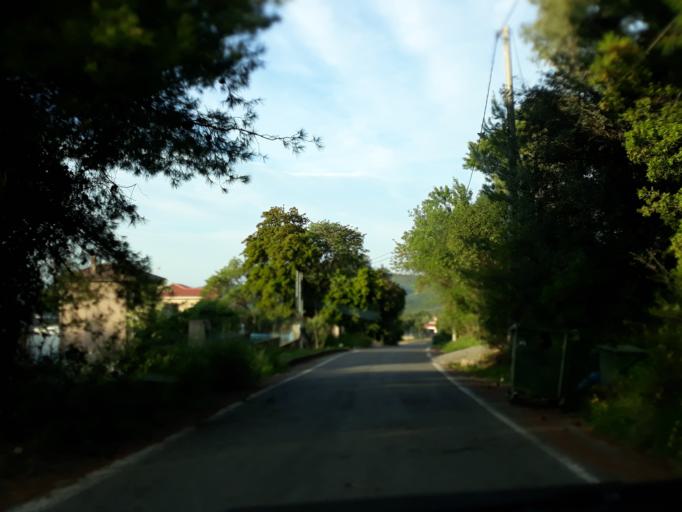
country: GR
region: Attica
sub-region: Nomarchia Anatolikis Attikis
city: Afidnes
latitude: 38.2294
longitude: 23.7864
